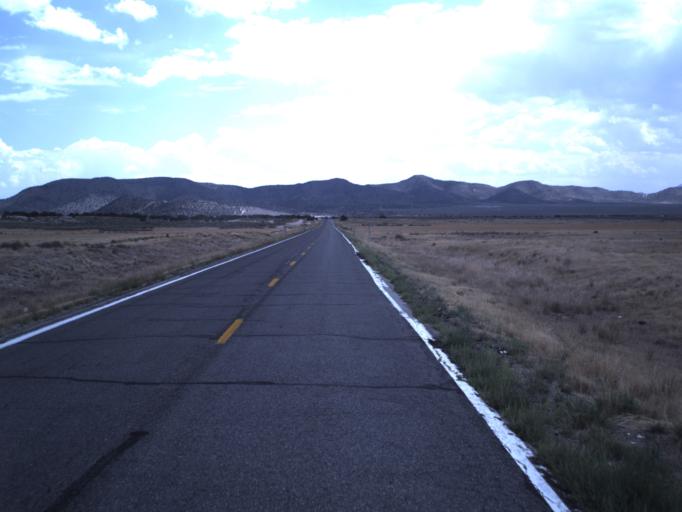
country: US
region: Utah
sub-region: Utah County
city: Eagle Mountain
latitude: 40.2433
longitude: -112.2085
